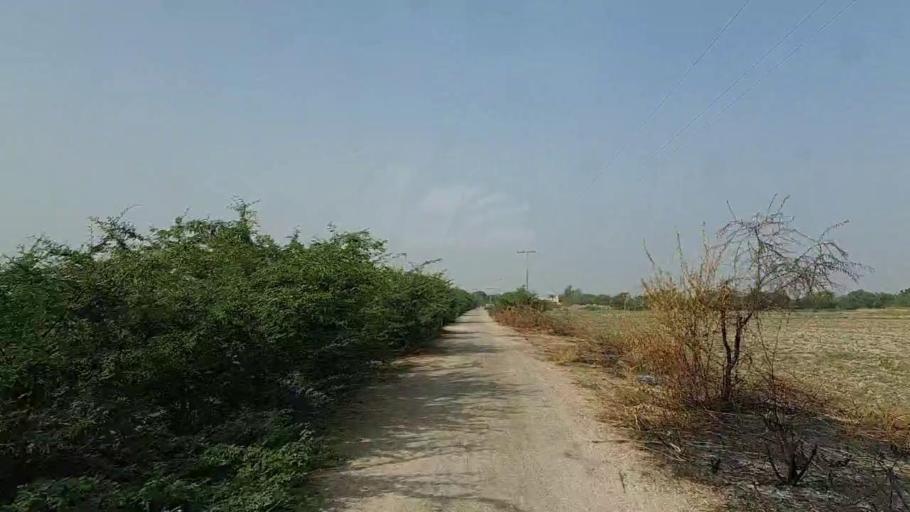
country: PK
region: Sindh
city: Naukot
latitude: 24.7615
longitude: 69.3373
